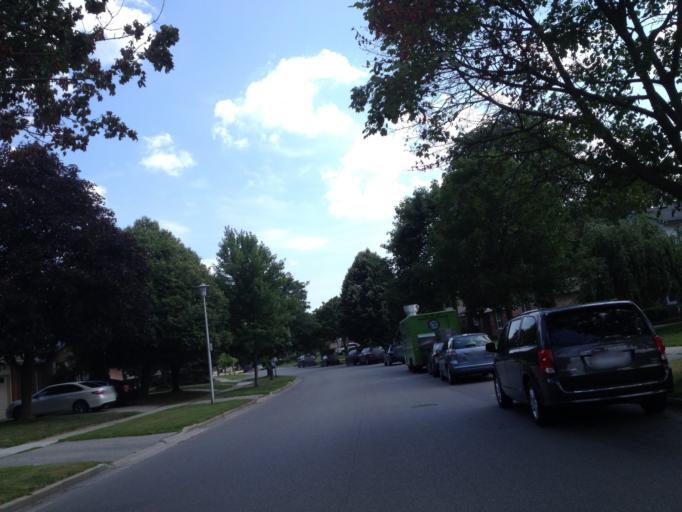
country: CA
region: Ontario
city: London
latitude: 43.0089
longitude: -81.3206
